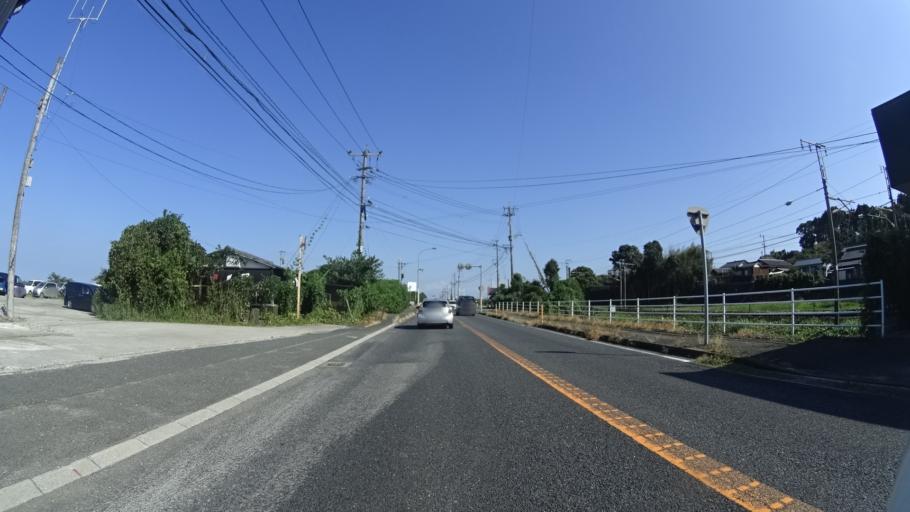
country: JP
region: Fukuoka
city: Shiida
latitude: 33.6360
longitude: 131.0742
